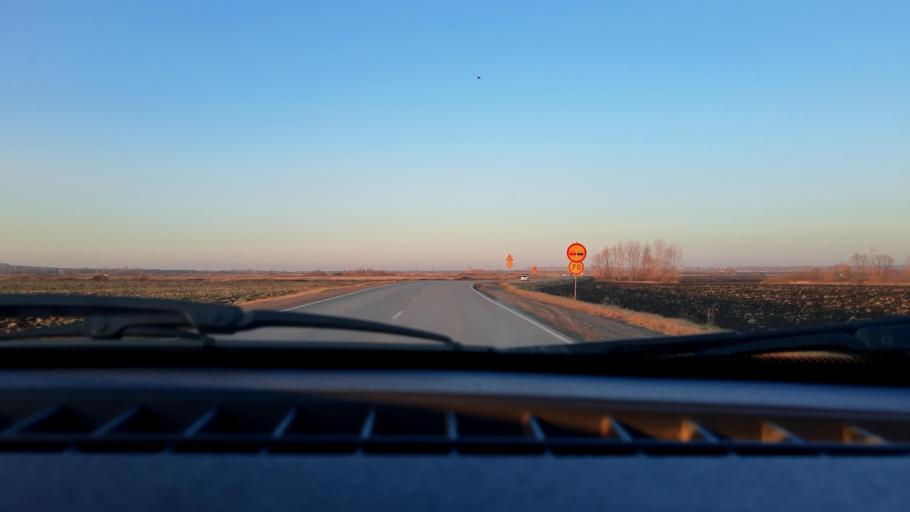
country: RU
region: Bashkortostan
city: Ufa
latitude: 54.8031
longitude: 55.9639
